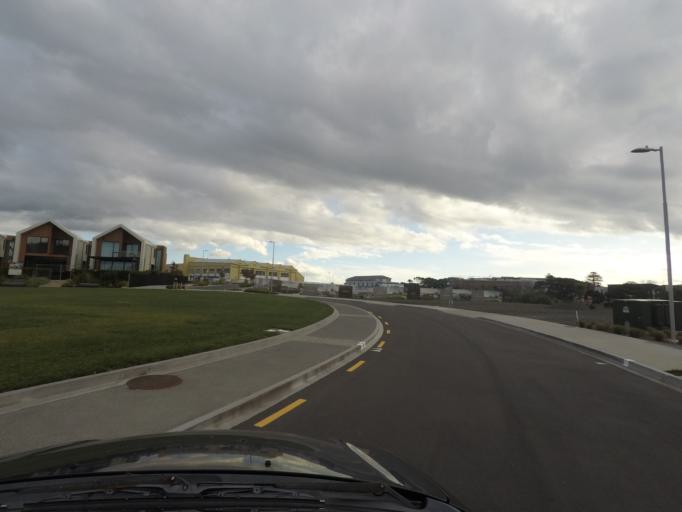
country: NZ
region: Auckland
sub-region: Auckland
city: North Shore
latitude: -36.7880
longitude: 174.6698
